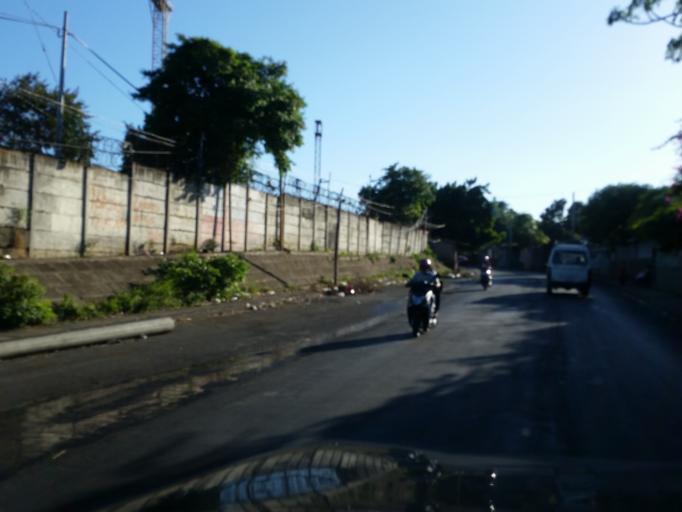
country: NI
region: Managua
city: Managua
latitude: 12.1329
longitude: -86.2848
